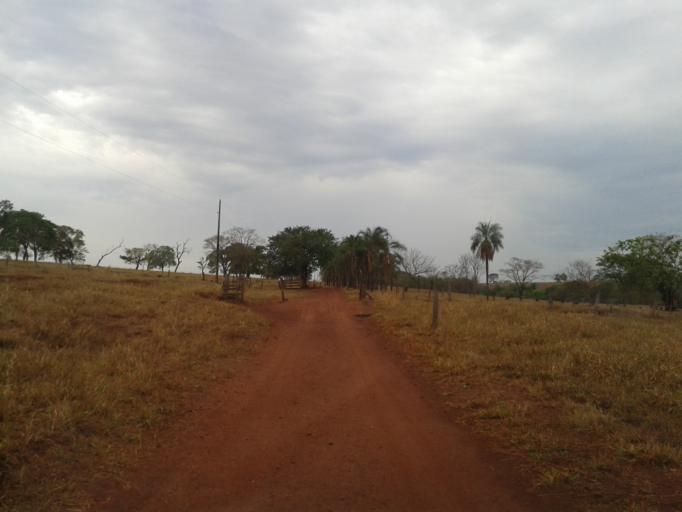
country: BR
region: Minas Gerais
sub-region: Santa Vitoria
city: Santa Vitoria
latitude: -18.8518
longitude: -49.8289
